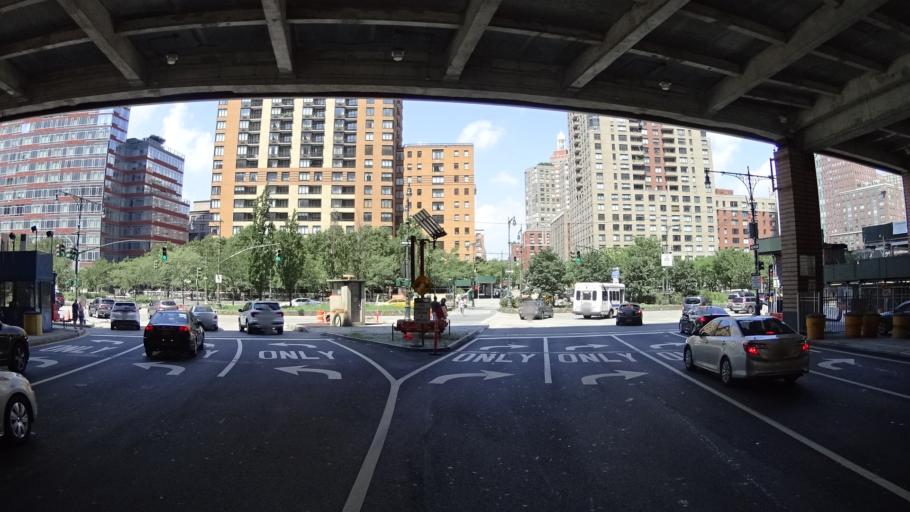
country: US
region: New York
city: New York City
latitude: 40.7074
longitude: -74.0152
